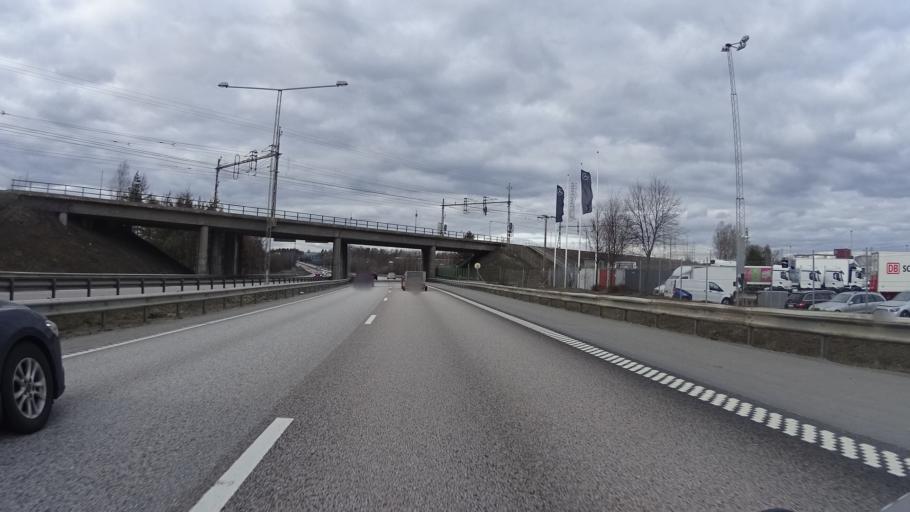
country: SE
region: Stockholm
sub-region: Sodertalje Kommun
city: Pershagen
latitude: 59.1651
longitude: 17.6499
